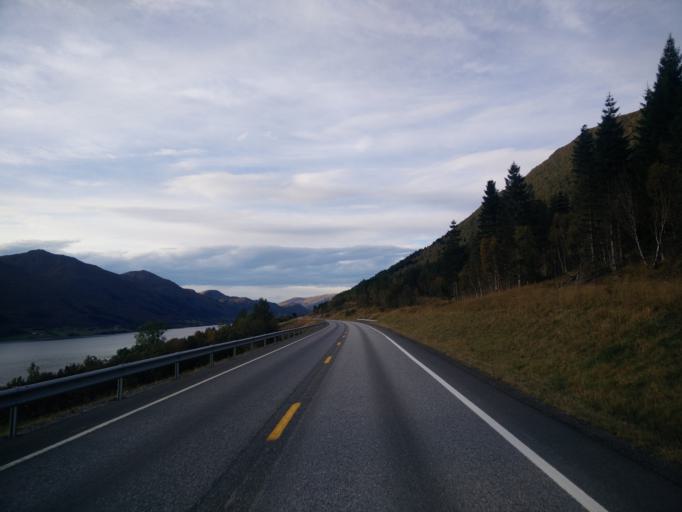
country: NO
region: More og Romsdal
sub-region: Gjemnes
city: Batnfjordsora
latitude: 62.9434
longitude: 7.7433
